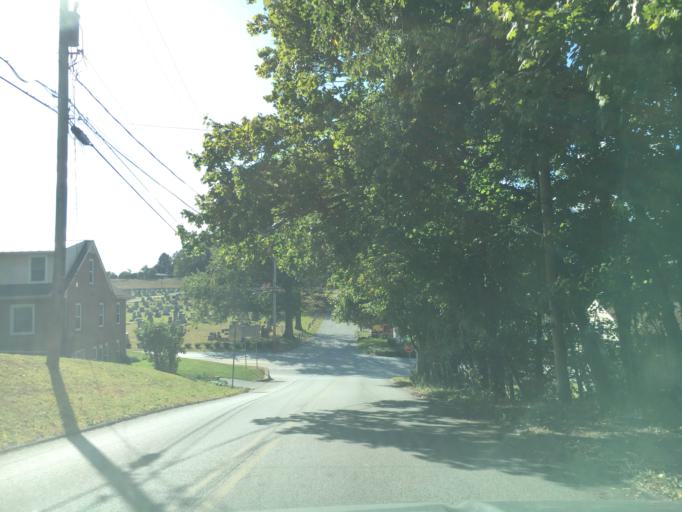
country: US
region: Pennsylvania
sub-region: York County
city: East York
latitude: 40.0023
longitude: -76.6824
